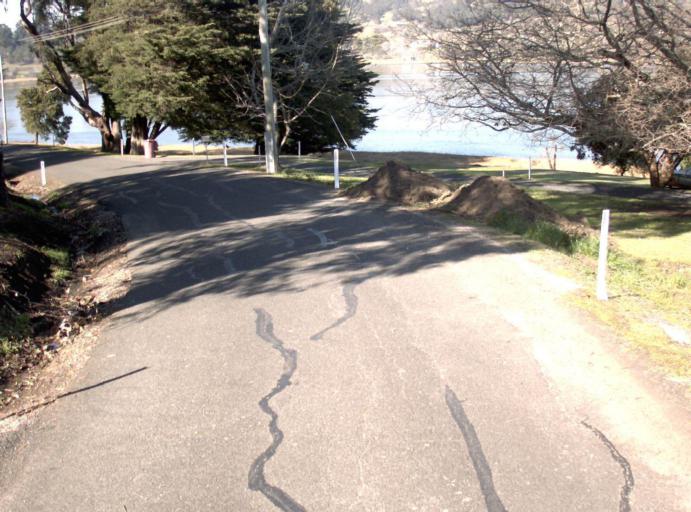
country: AU
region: Tasmania
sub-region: Launceston
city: Mayfield
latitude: -41.3145
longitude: 146.9968
